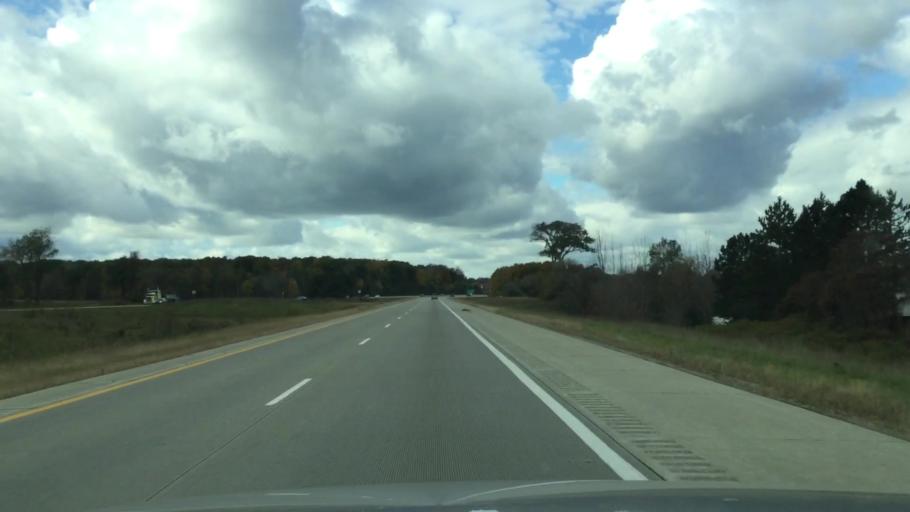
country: US
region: Michigan
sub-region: Genesee County
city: Davison
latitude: 43.0175
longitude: -83.4237
